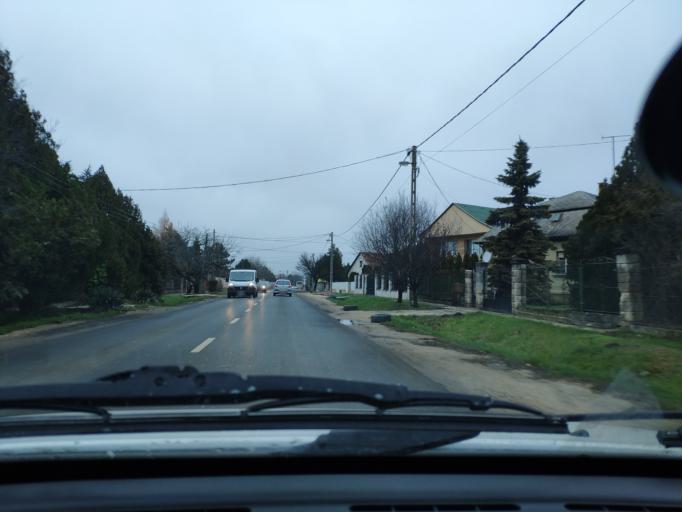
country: HU
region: Pest
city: Soskut
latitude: 47.3994
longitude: 18.8389
